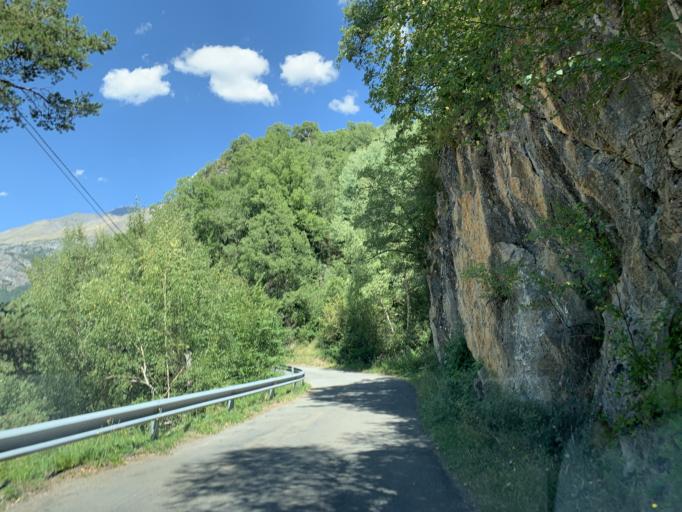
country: ES
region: Aragon
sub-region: Provincia de Huesca
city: Hoz de Jaca
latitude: 42.7075
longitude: -0.3041
